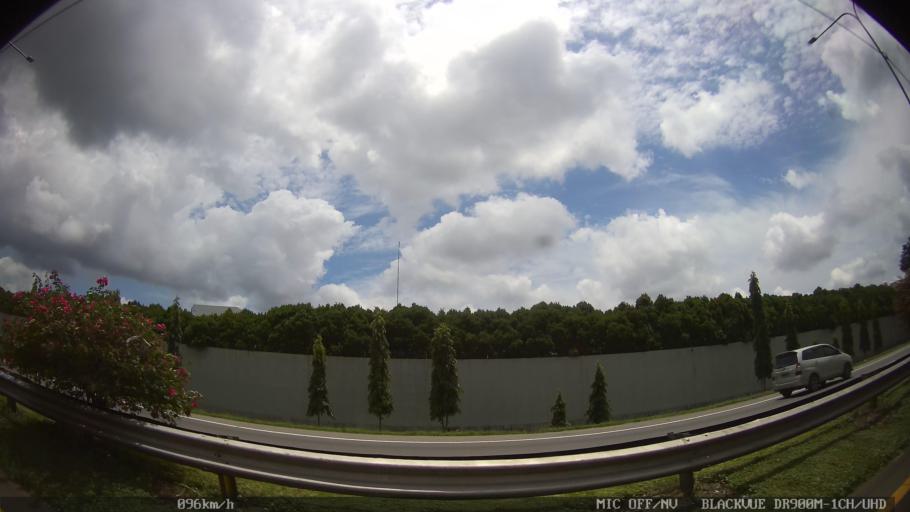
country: ID
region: North Sumatra
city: Medan
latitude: 3.6090
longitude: 98.7222
